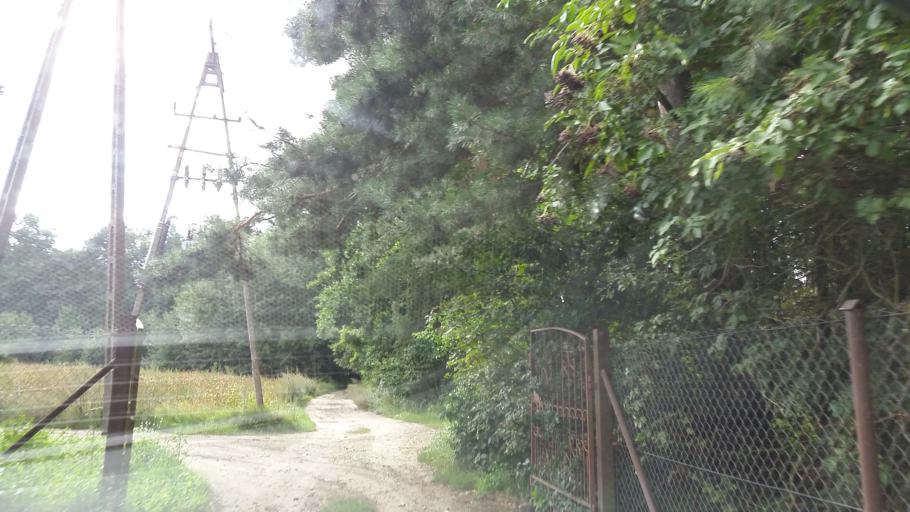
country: PL
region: West Pomeranian Voivodeship
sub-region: Powiat choszczenski
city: Choszczno
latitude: 53.2227
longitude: 15.3844
